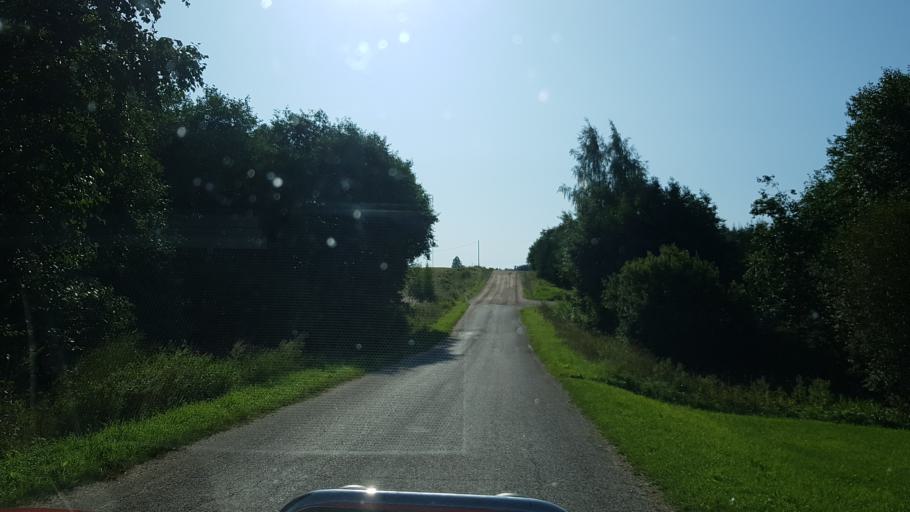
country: LV
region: Apes Novads
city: Ape
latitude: 57.6069
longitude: 26.8423
